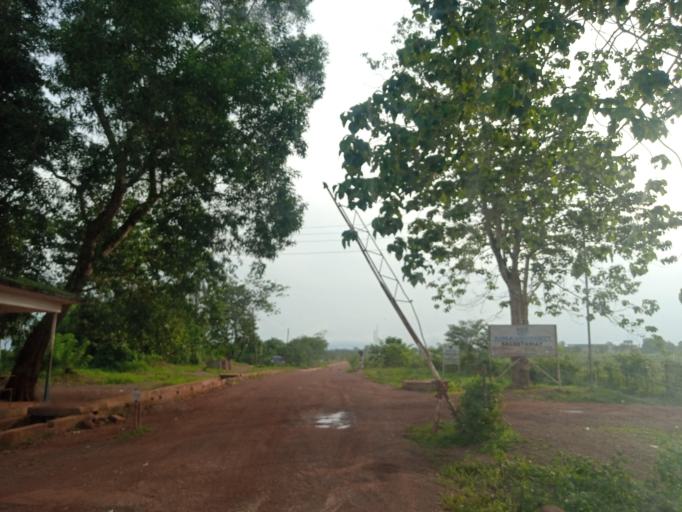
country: SL
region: Southern Province
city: Largo
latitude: 8.1160
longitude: -12.0590
